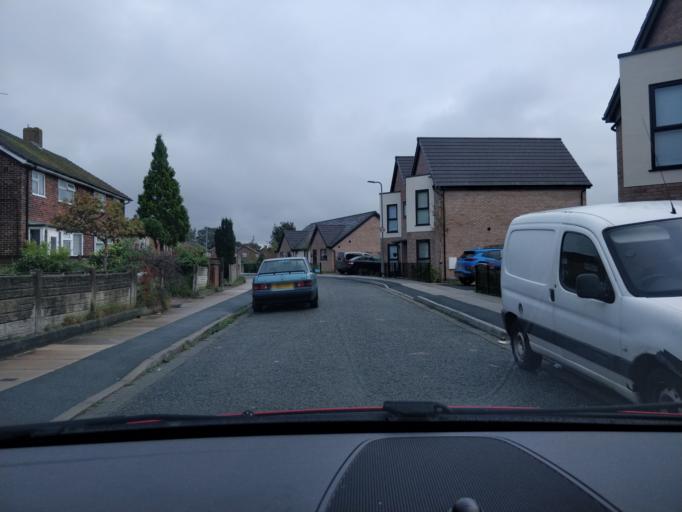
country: GB
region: England
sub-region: Sefton
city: Southport
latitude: 53.6044
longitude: -3.0259
